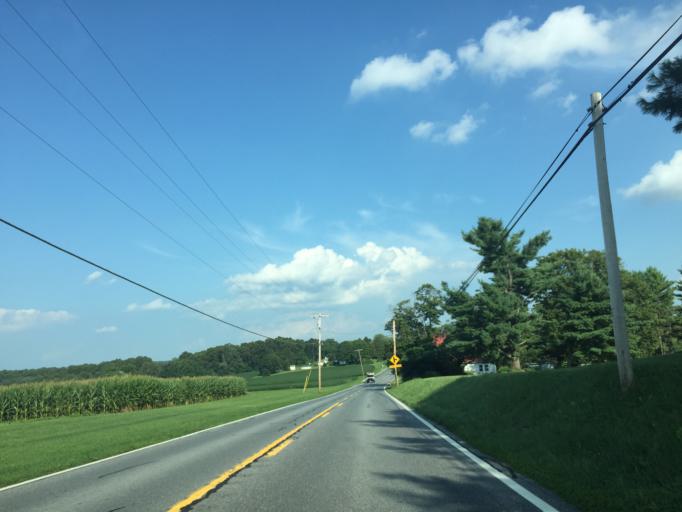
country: US
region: Maryland
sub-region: Carroll County
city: Hampstead
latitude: 39.5995
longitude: -76.7677
